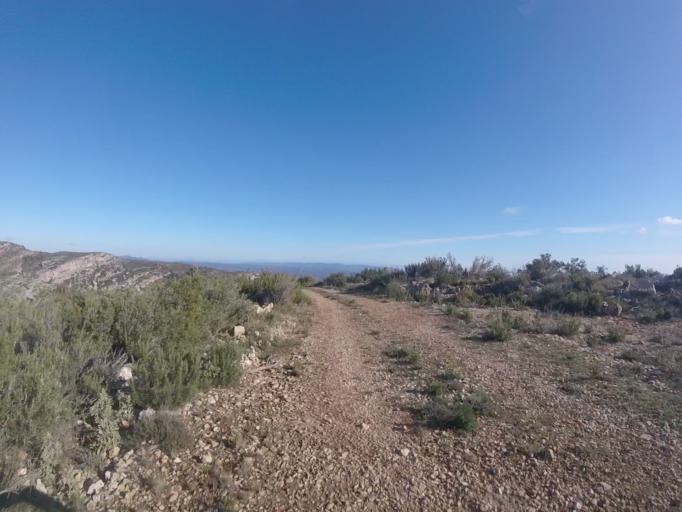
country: ES
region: Valencia
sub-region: Provincia de Castello
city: Sarratella
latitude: 40.3005
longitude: 0.0401
